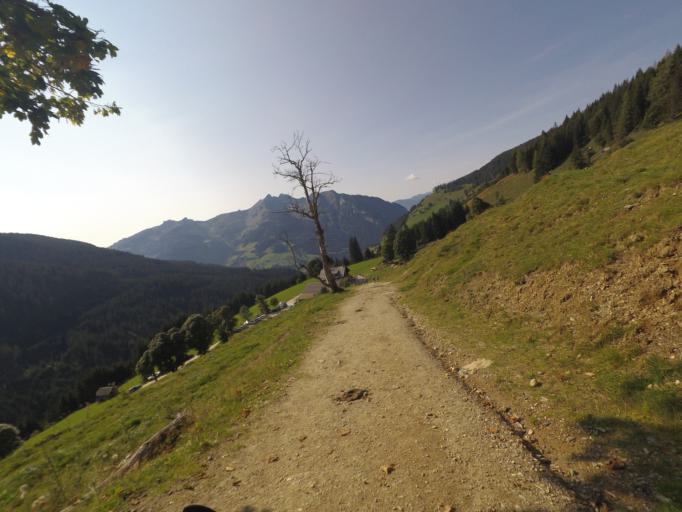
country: AT
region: Salzburg
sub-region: Politischer Bezirk Sankt Johann im Pongau
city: Kleinarl
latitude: 47.2729
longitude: 13.2544
